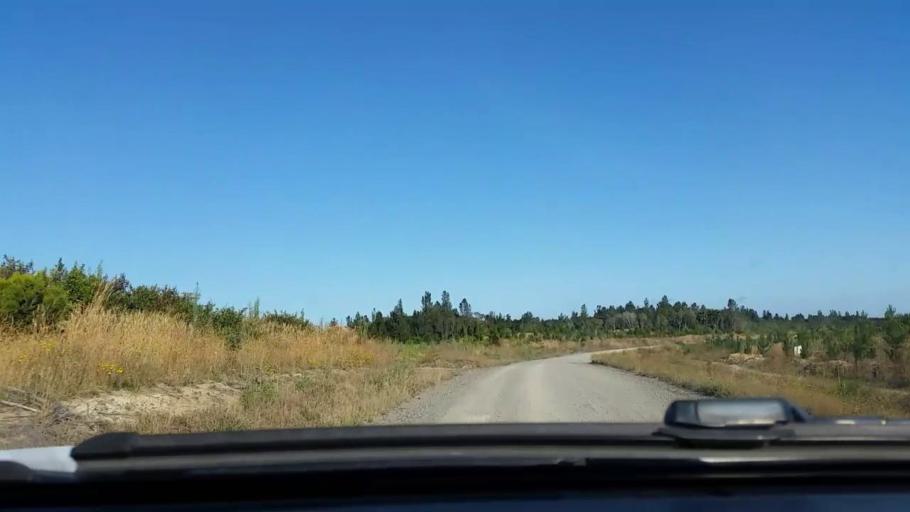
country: NZ
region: Bay of Plenty
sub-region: Kawerau District
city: Kawerau
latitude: -37.9989
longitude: 176.5415
